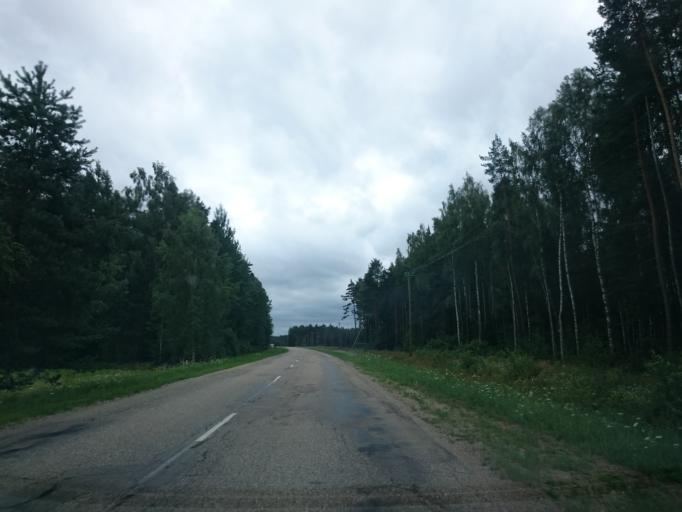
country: LV
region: Pavilostas
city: Pavilosta
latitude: 56.8057
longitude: 21.2266
